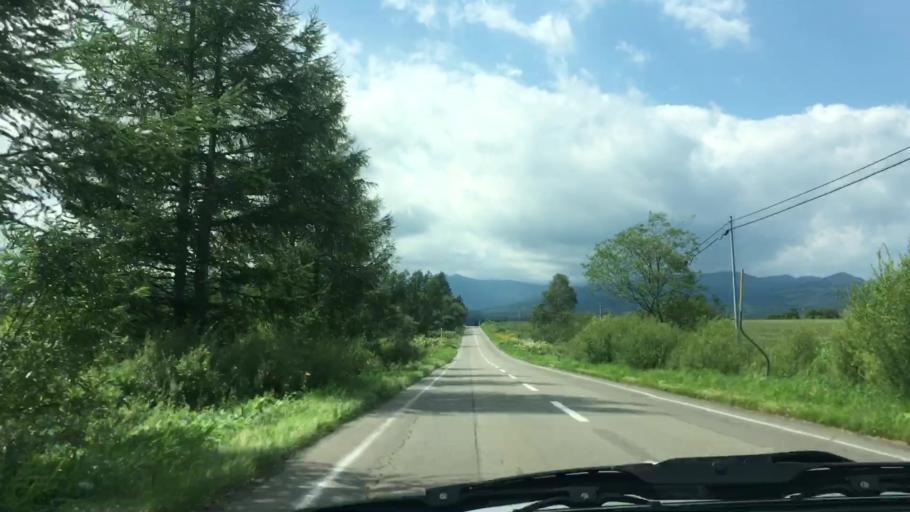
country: JP
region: Hokkaido
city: Otofuke
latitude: 43.2790
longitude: 143.3499
